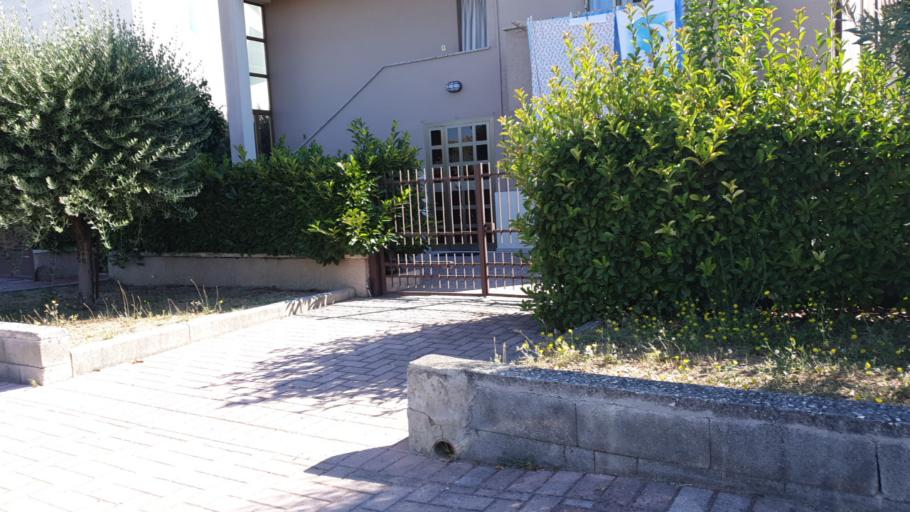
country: IT
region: Umbria
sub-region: Provincia di Perugia
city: Foligno
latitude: 42.9554
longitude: 12.6884
